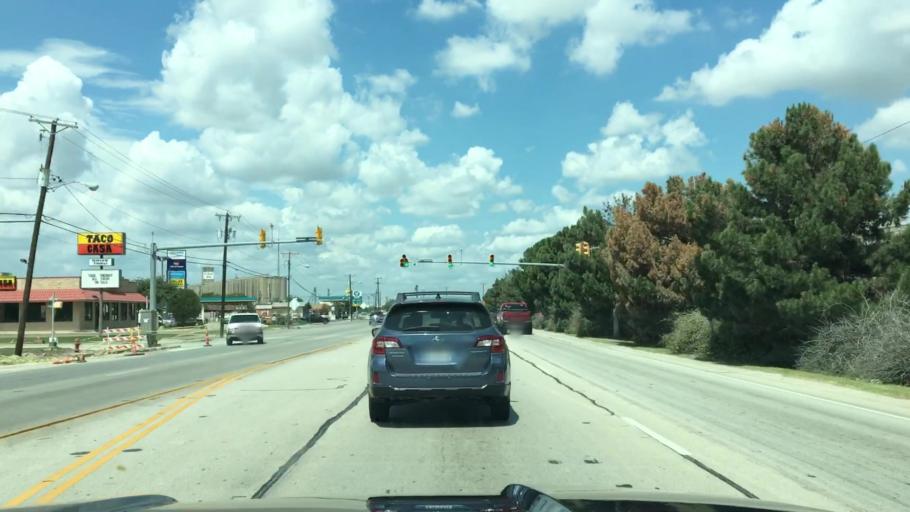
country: US
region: Texas
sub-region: Tarrant County
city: Saginaw
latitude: 32.8531
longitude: -97.3608
